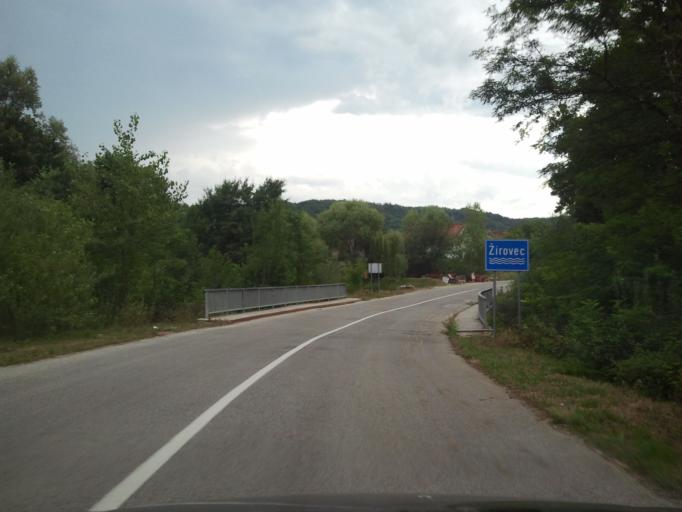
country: HR
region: Sisacko-Moslavacka
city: Glina
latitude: 45.4850
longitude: 16.0005
